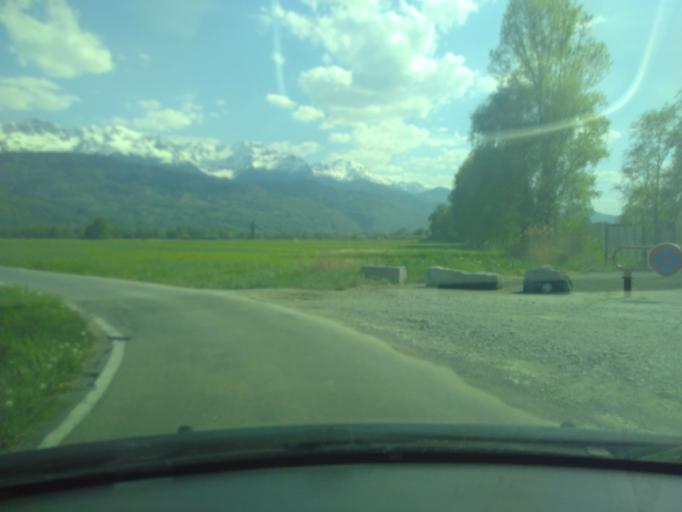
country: FR
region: Rhone-Alpes
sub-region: Departement de l'Isere
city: Lumbin
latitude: 45.3007
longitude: 5.9078
